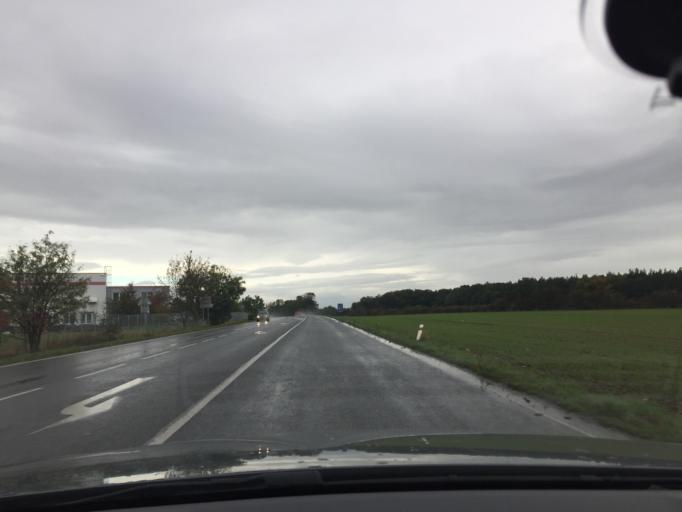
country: CZ
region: Central Bohemia
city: Odolena Voda
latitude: 50.2257
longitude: 14.4016
